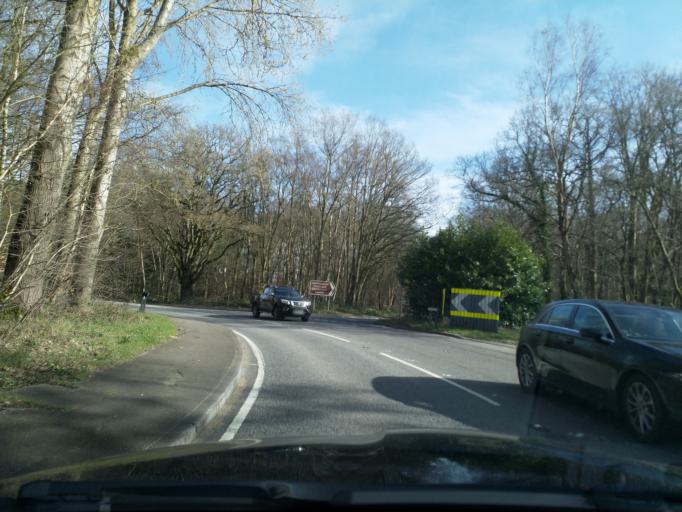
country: GB
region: England
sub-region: Hampshire
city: Aldershot
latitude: 51.2618
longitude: -0.7763
